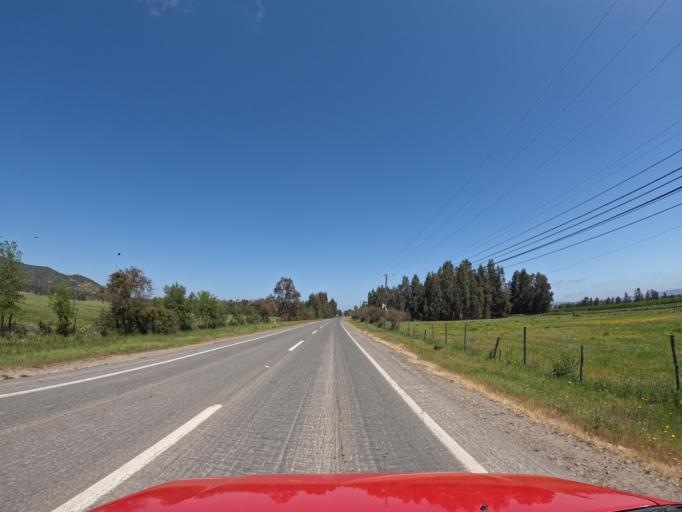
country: CL
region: O'Higgins
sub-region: Provincia de Colchagua
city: Santa Cruz
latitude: -34.7316
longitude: -71.6805
